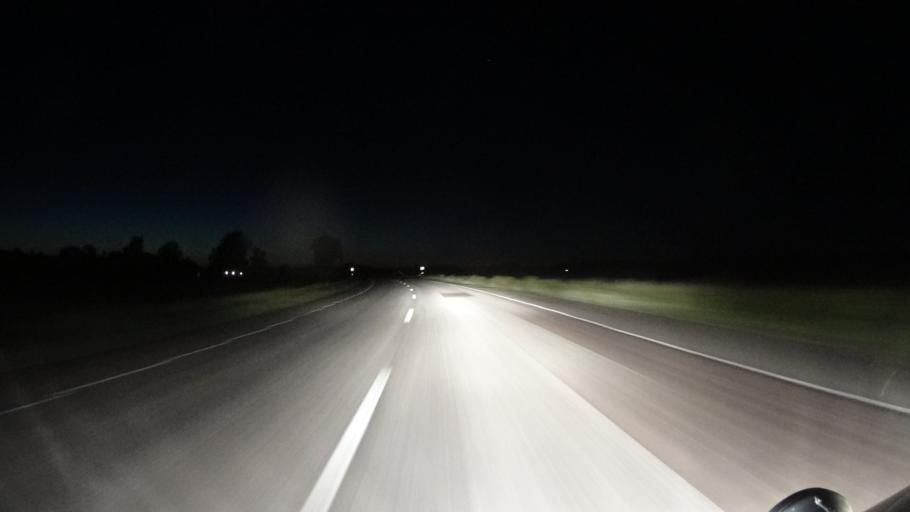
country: SE
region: OEstergoetland
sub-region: Odeshogs Kommun
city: OEdeshoeg
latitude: 58.2479
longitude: 14.7253
